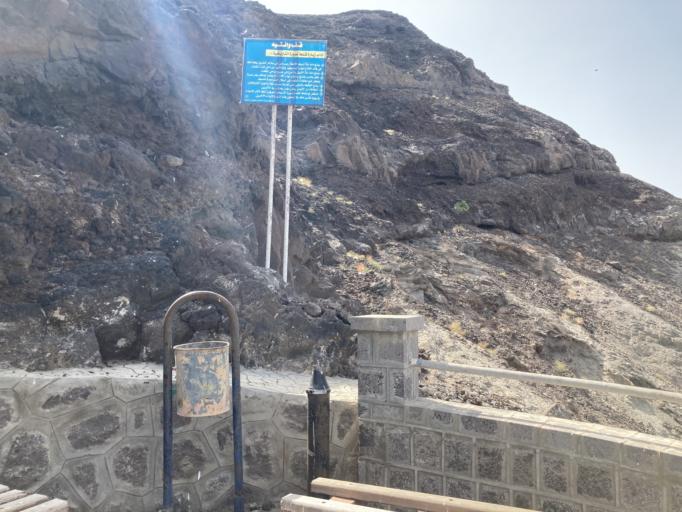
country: YE
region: Aden
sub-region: Craiter
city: Aden
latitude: 12.7810
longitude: 45.0496
